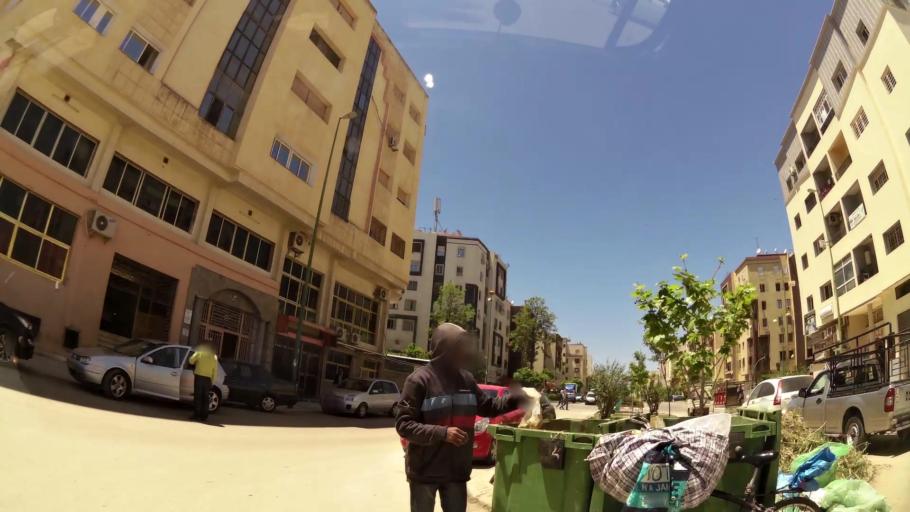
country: MA
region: Meknes-Tafilalet
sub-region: Meknes
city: Meknes
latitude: 33.8659
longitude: -5.5761
